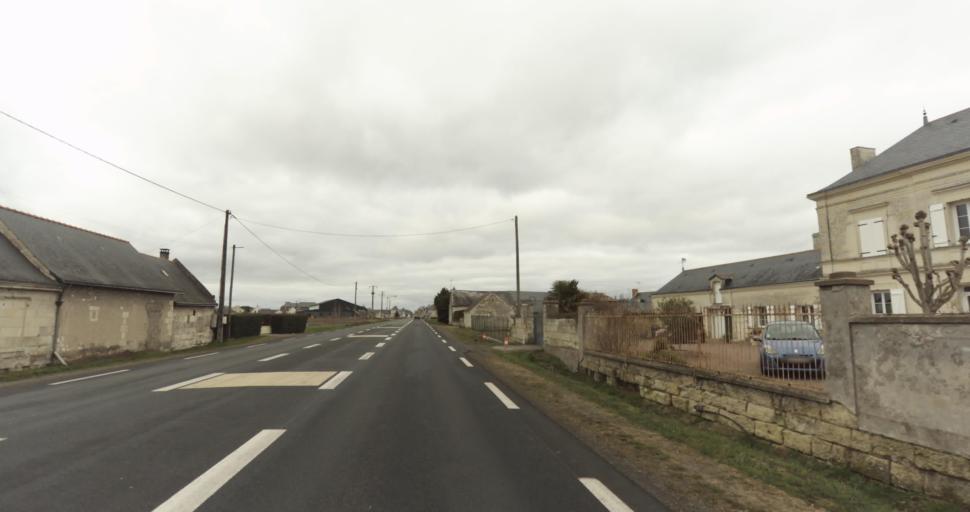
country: FR
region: Pays de la Loire
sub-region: Departement de Maine-et-Loire
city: Vivy
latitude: 47.3210
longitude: -0.0513
